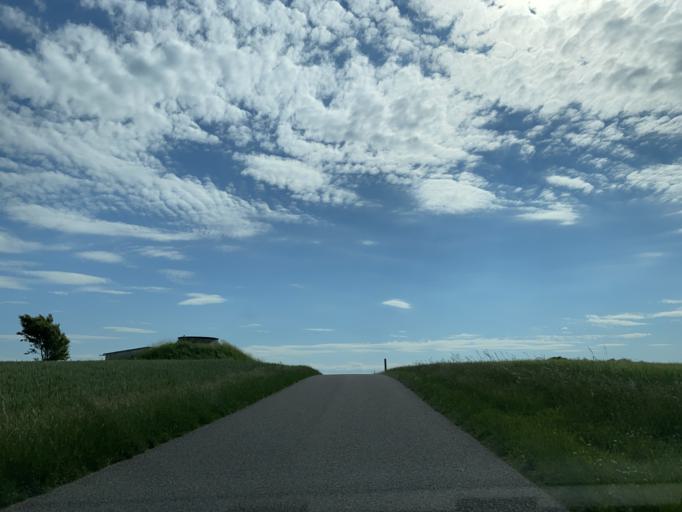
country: DK
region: Central Jutland
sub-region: Favrskov Kommune
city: Hammel
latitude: 56.2114
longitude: 9.8856
